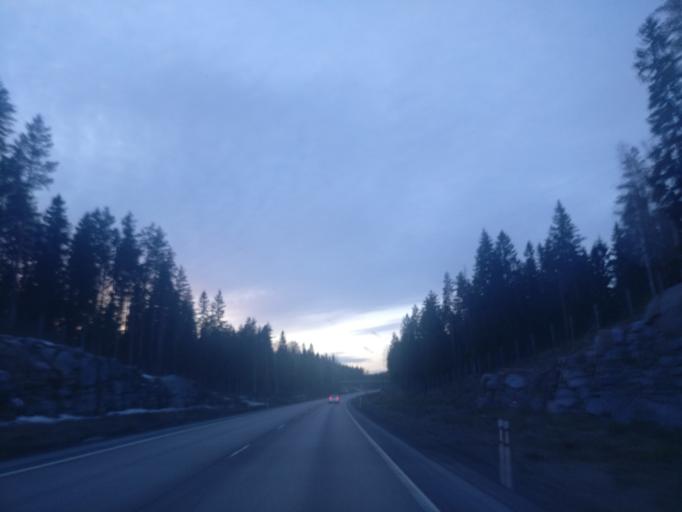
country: FI
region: Central Finland
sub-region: Jyvaeskylae
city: Saeynaetsalo
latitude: 62.1950
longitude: 25.8967
